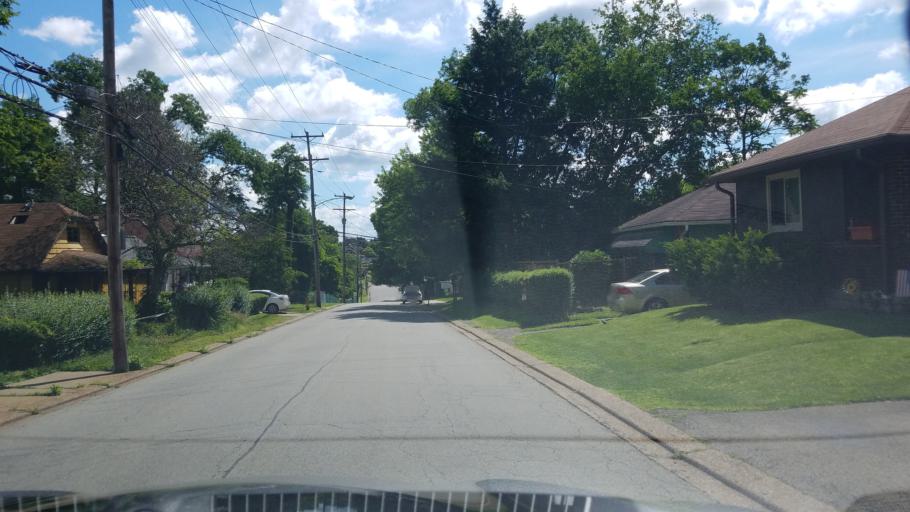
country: US
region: Pennsylvania
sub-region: Allegheny County
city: Swissvale
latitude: 40.4225
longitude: -79.8759
